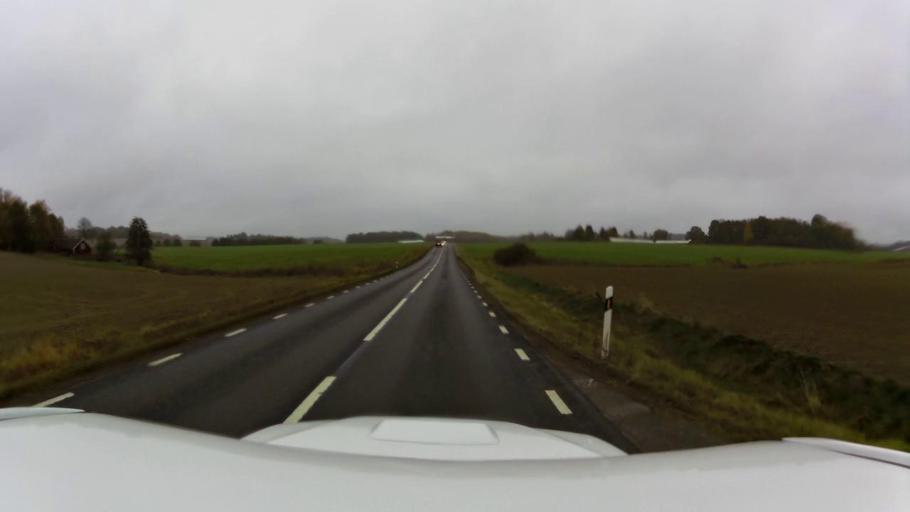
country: SE
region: OEstergoetland
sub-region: Linkopings Kommun
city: Linghem
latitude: 58.3931
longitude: 15.7736
